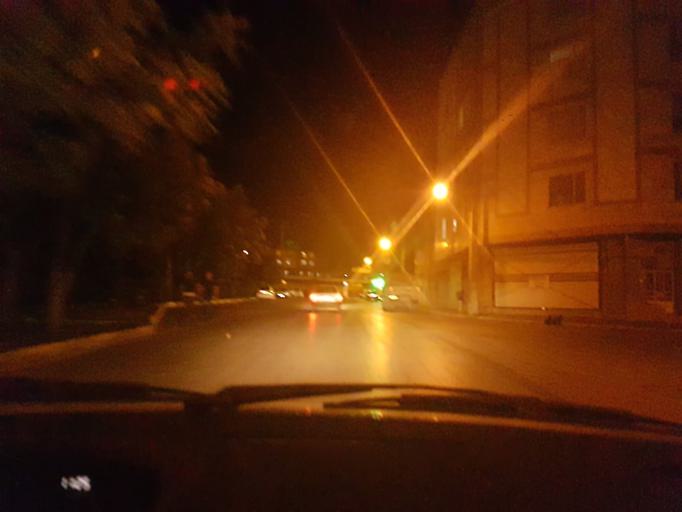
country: IR
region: Markazi
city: Arak
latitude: 34.0725
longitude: 49.6756
